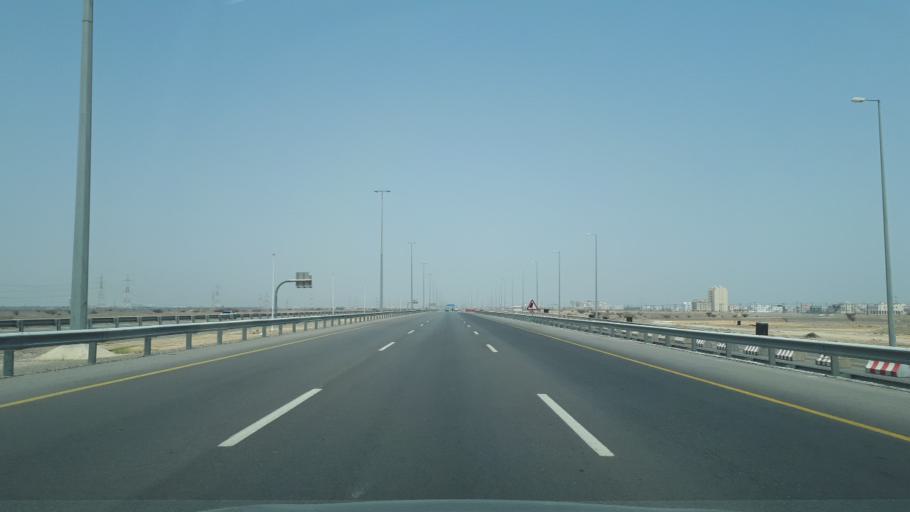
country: OM
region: Muhafazat Masqat
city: As Sib al Jadidah
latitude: 23.6297
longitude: 58.0695
